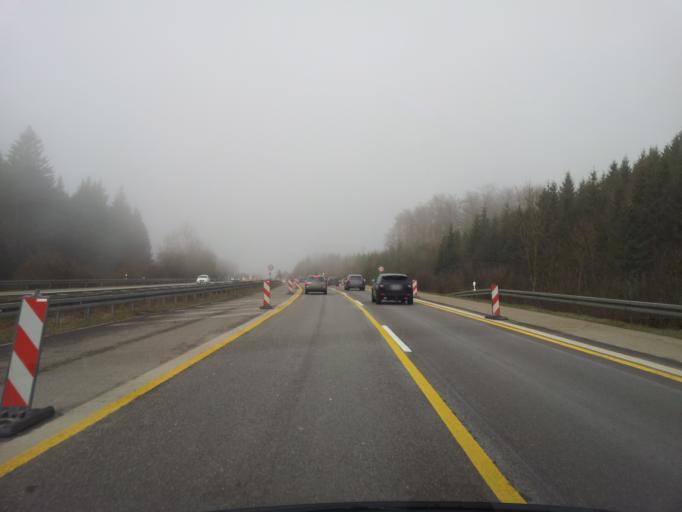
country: DE
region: Baden-Wuerttemberg
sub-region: Freiburg Region
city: Immendingen
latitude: 47.8921
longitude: 8.7227
